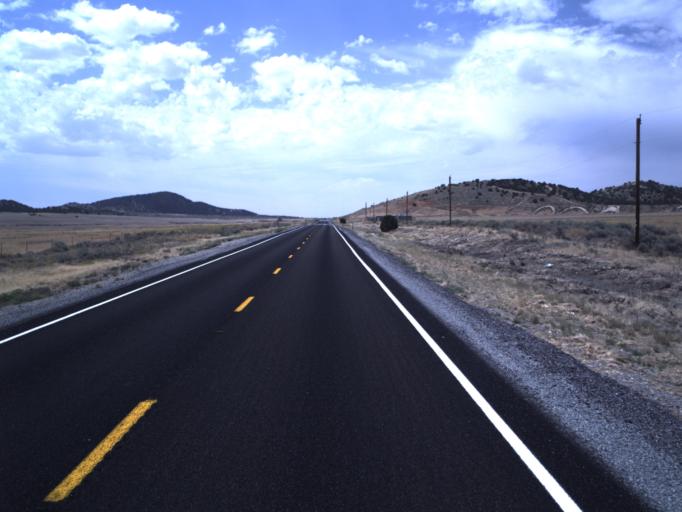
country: US
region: Utah
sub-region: Utah County
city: Eagle Mountain
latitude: 40.2445
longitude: -112.1387
